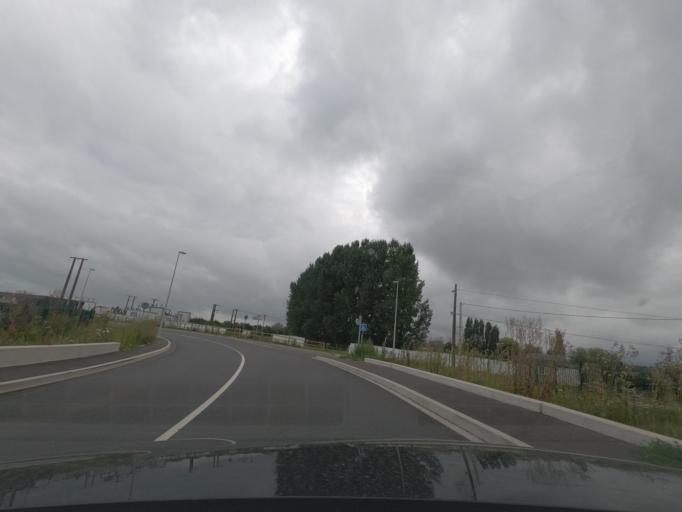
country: FR
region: Haute-Normandie
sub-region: Departement de la Seine-Maritime
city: Forges-les-Eaux
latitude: 49.6122
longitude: 1.5574
